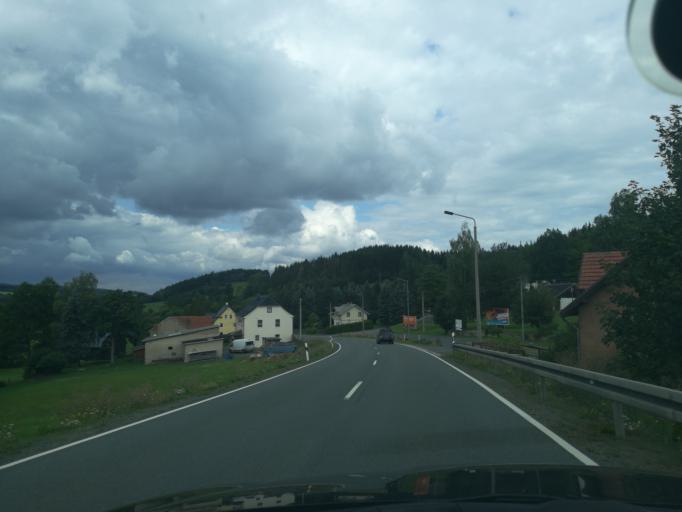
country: DE
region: Saxony
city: Adorf
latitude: 50.3627
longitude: 12.2240
